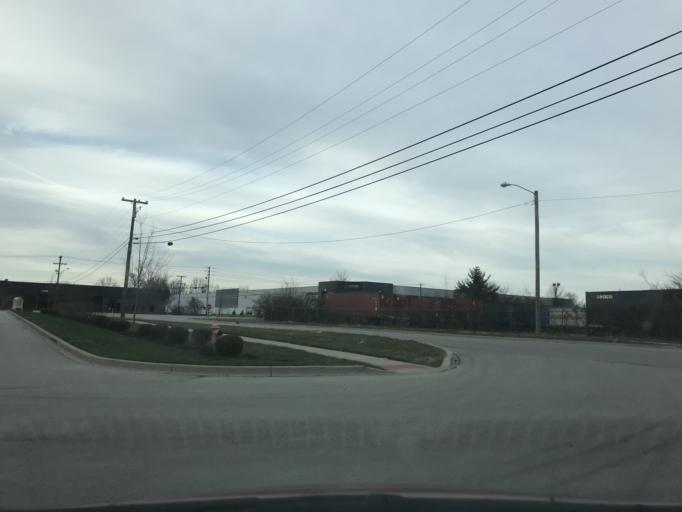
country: US
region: Kentucky
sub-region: Jefferson County
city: West Buechel
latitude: 38.1852
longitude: -85.6791
